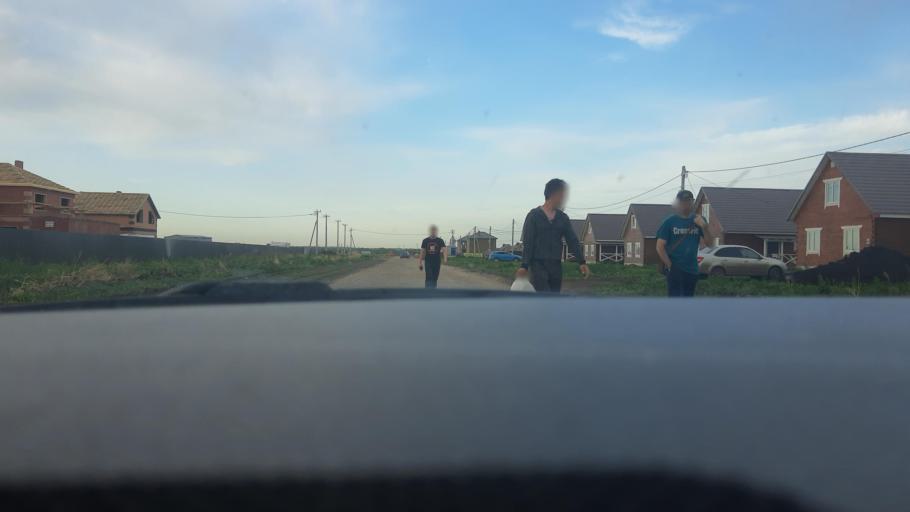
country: RU
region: Bashkortostan
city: Kabakovo
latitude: 54.6297
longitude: 56.1364
